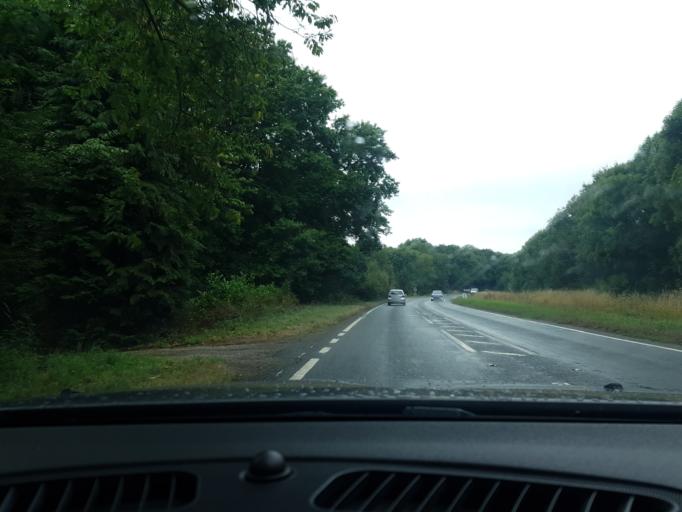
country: GB
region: England
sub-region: Hampshire
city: Odiham
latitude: 51.2468
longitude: -0.8902
